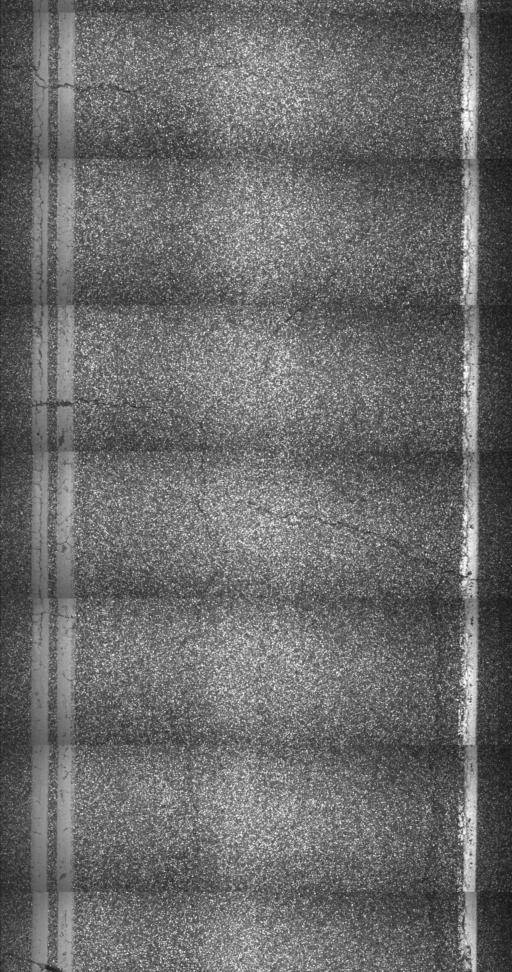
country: US
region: Vermont
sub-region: Windham County
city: West Brattleboro
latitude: 42.9077
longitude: -72.6028
